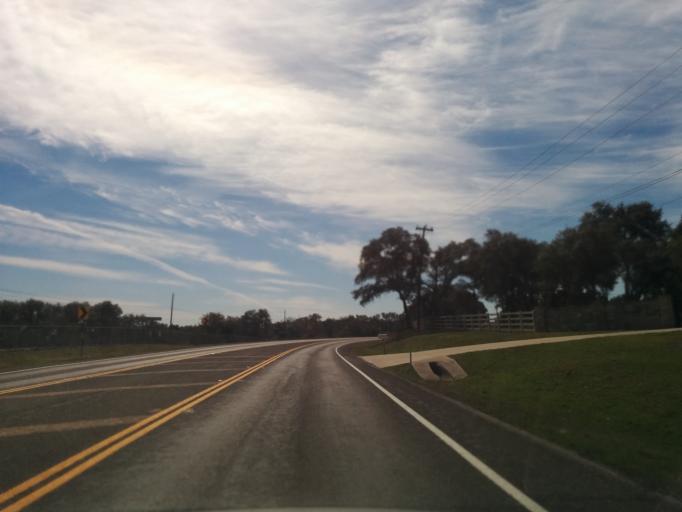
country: US
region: Texas
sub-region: Bexar County
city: Fair Oaks Ranch
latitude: 29.7193
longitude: -98.6236
